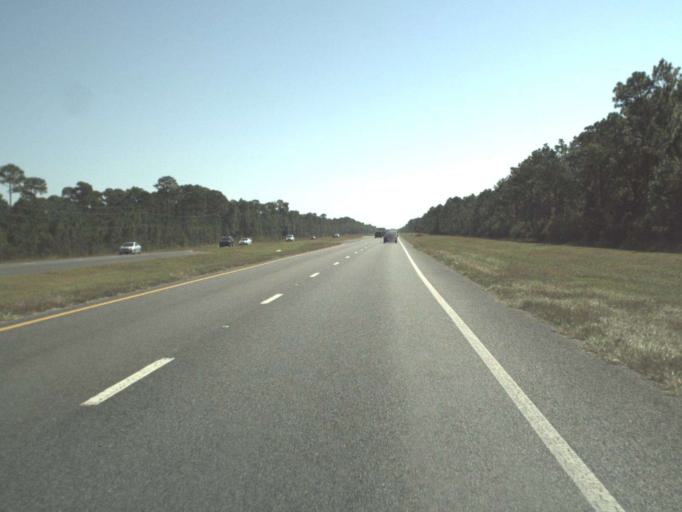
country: US
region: Florida
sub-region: Walton County
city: Seaside
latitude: 30.3723
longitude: -86.2075
